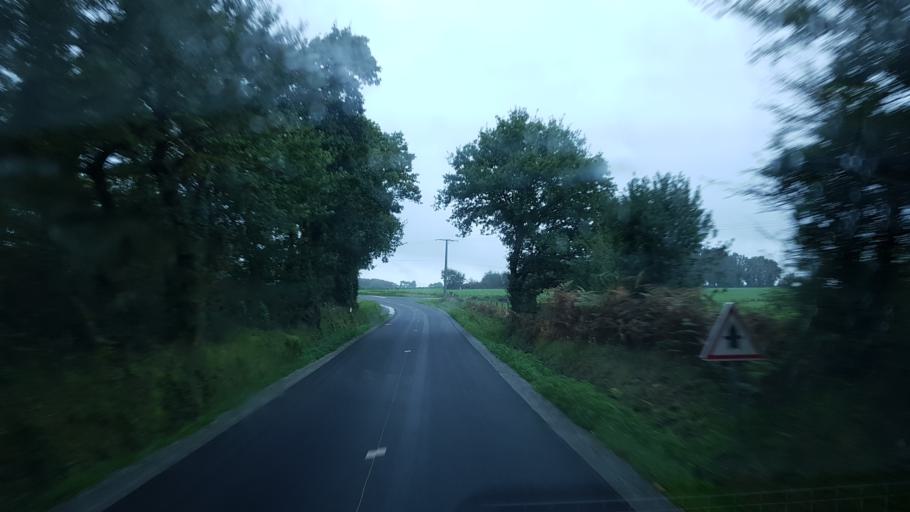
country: FR
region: Brittany
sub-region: Departement du Morbihan
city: Theix
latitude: 47.6532
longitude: -2.6300
